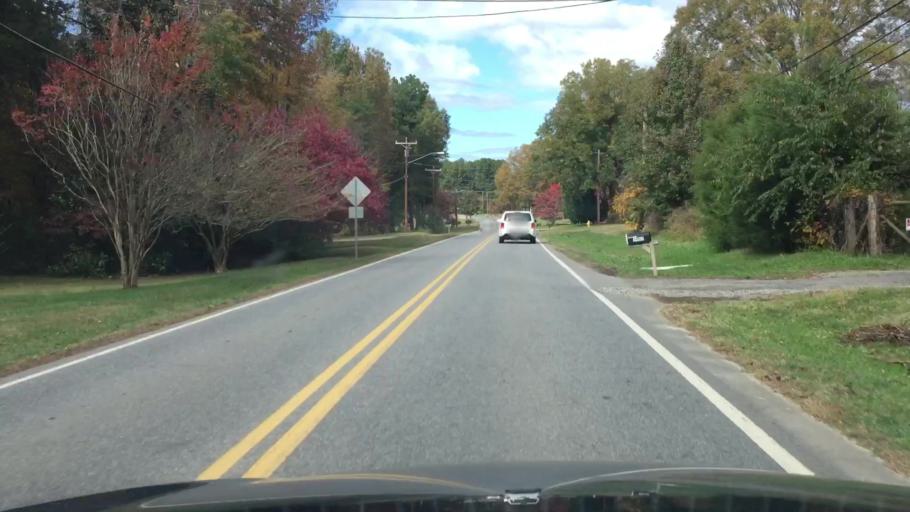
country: US
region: North Carolina
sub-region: Iredell County
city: Mooresville
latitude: 35.5526
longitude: -80.8097
